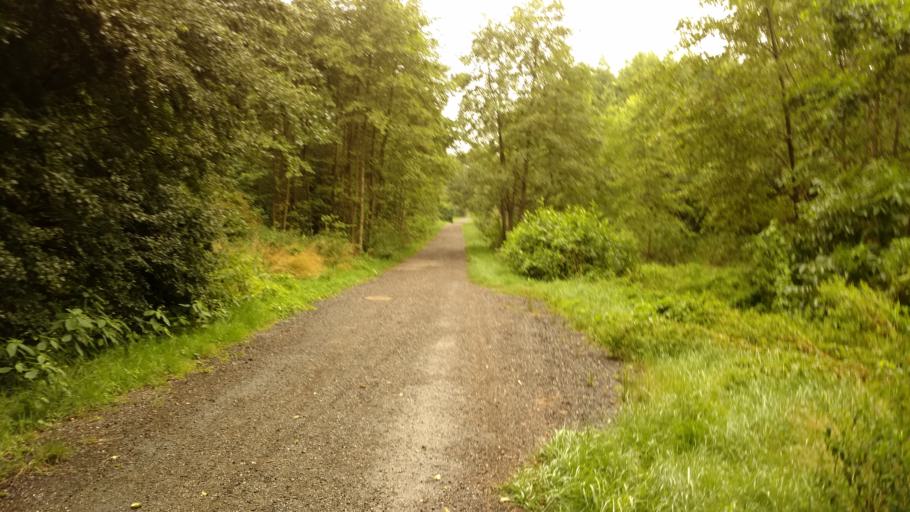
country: PL
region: Lesser Poland Voivodeship
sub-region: Powiat krakowski
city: Michalowice
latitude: 50.1331
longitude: 19.9738
